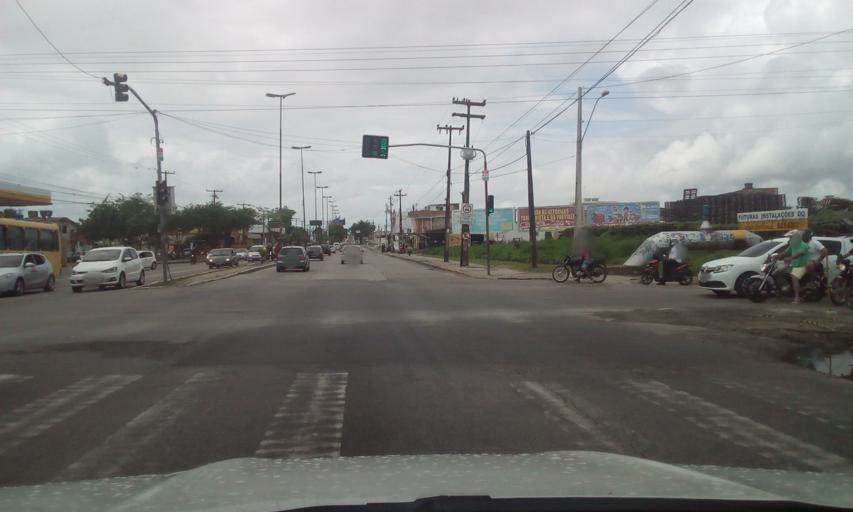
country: BR
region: Pernambuco
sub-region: Recife
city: Recife
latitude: -8.1077
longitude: -34.9272
